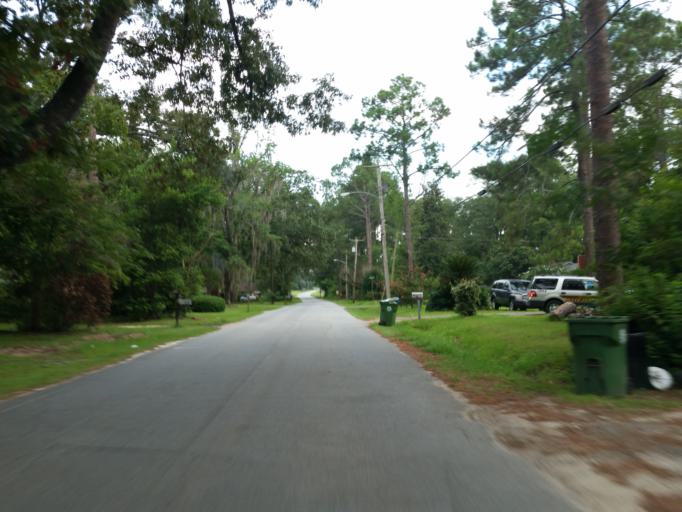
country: US
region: Georgia
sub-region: Cook County
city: Adel
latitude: 31.1280
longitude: -83.4172
